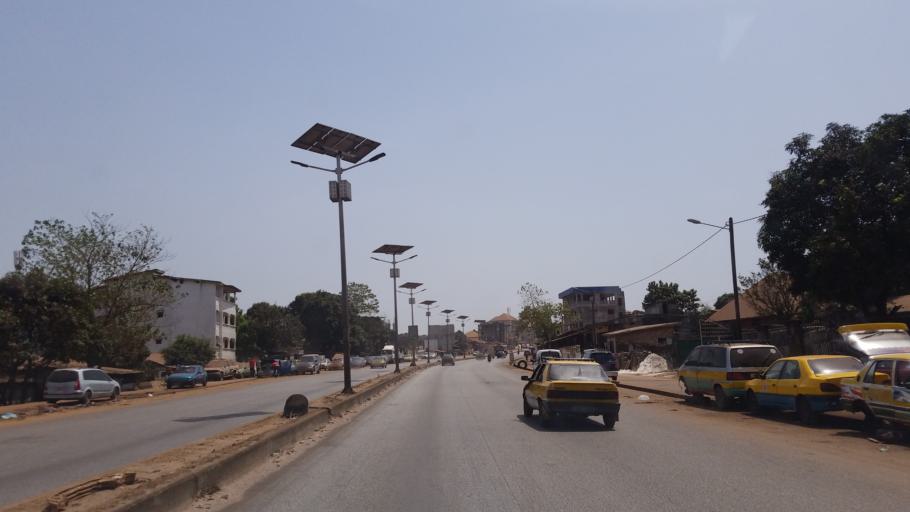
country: GN
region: Conakry
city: Conakry
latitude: 9.6462
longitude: -13.5855
